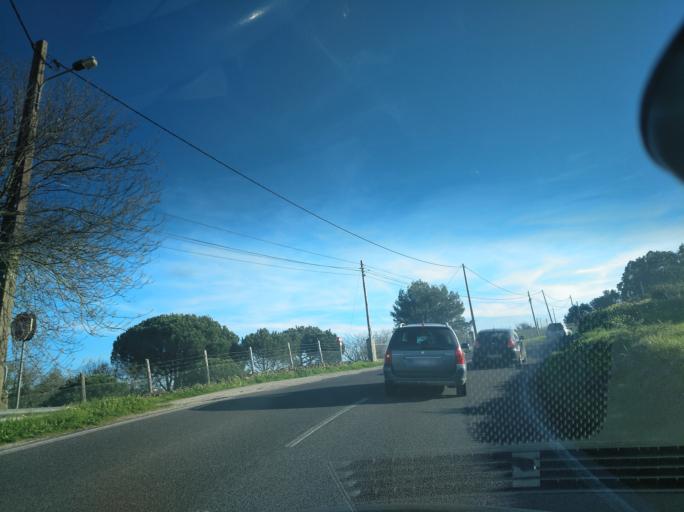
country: PT
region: Lisbon
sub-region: Sintra
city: Pero Pinheiro
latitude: 38.8822
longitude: -9.3300
